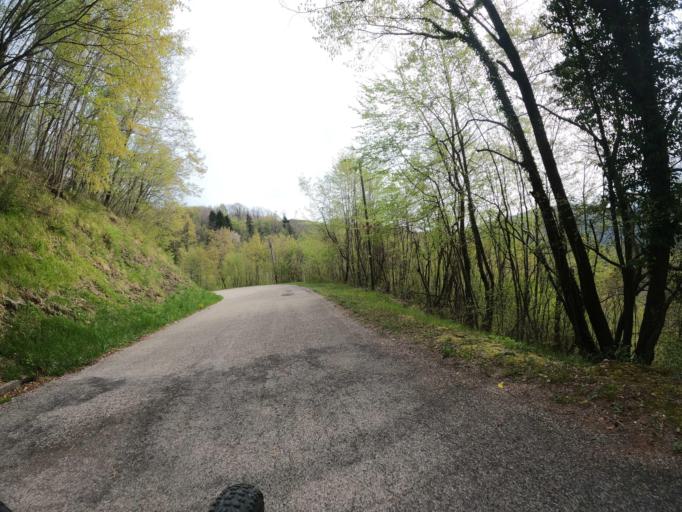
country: IT
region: Friuli Venezia Giulia
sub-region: Provincia di Udine
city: Clodig
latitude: 46.1413
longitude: 13.5986
